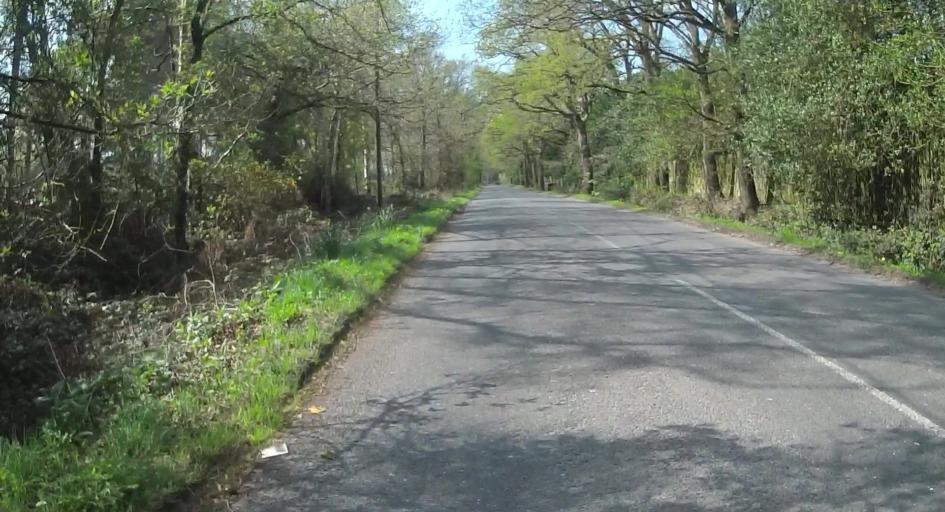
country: GB
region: England
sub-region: Hampshire
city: Tadley
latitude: 51.3719
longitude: -1.1245
